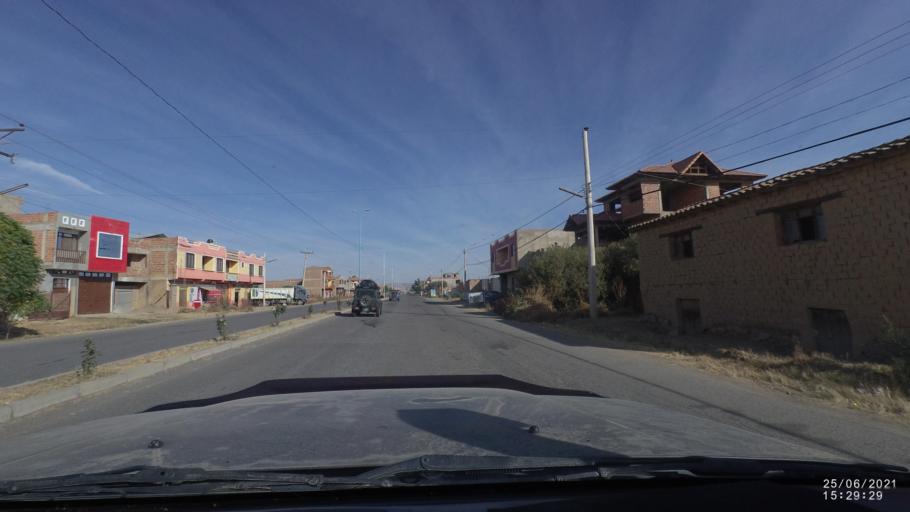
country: BO
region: Cochabamba
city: Cliza
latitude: -17.5730
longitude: -65.9349
